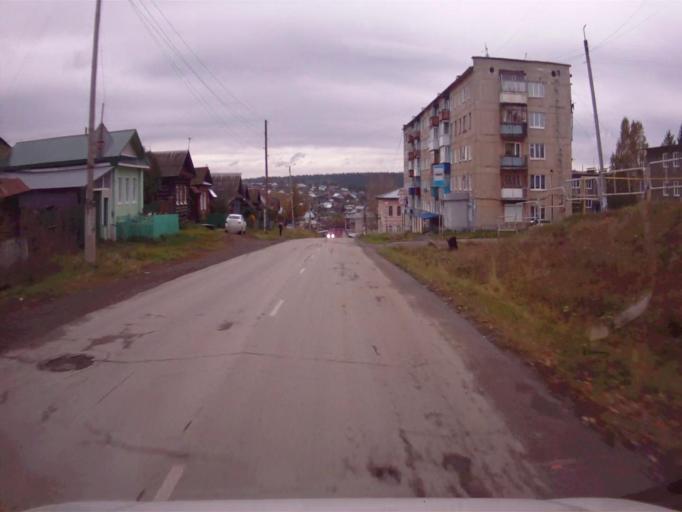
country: RU
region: Chelyabinsk
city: Nyazepetrovsk
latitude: 56.0549
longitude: 59.6044
